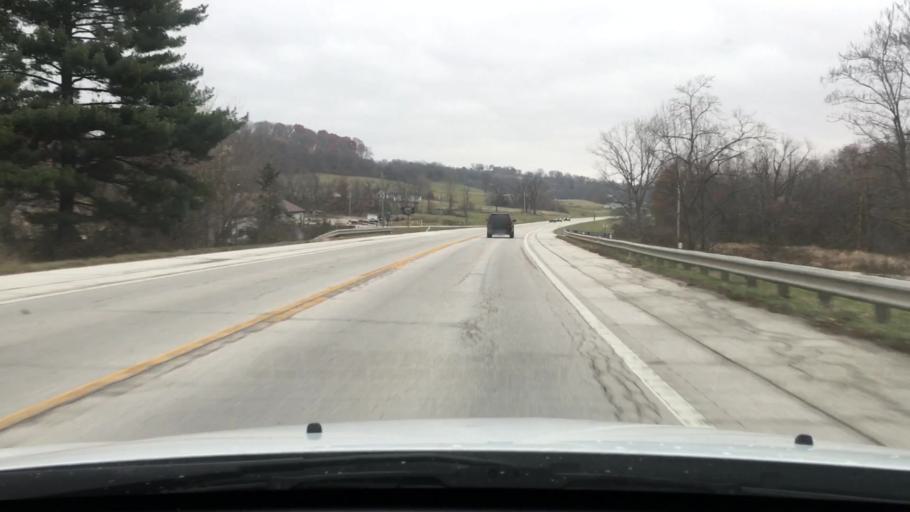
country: US
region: Missouri
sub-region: Pike County
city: Louisiana
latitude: 39.4474
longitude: -91.0733
